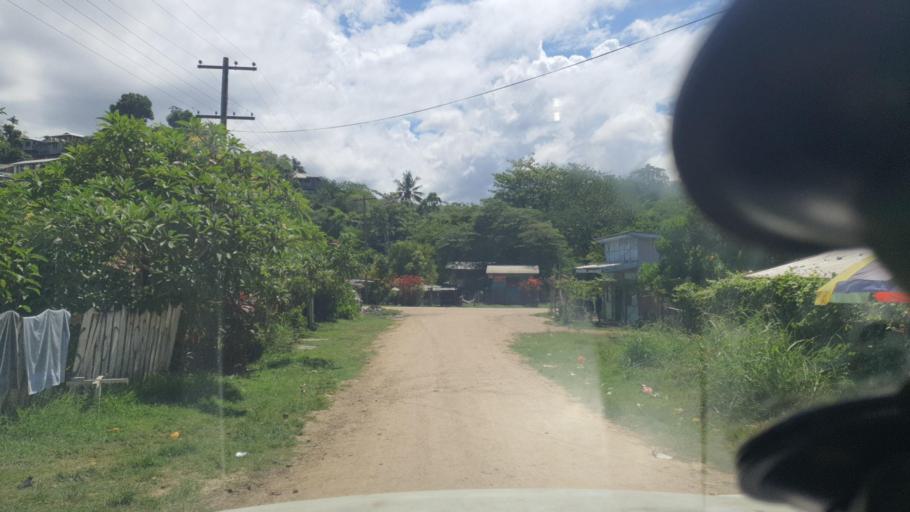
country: SB
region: Guadalcanal
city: Honiara
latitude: -9.4447
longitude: 159.9596
